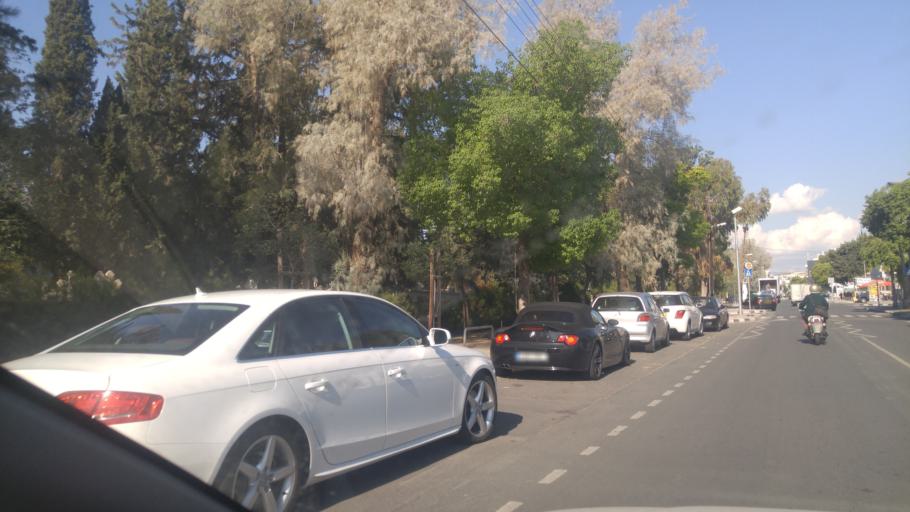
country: CY
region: Limassol
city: Limassol
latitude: 34.6908
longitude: 33.0576
